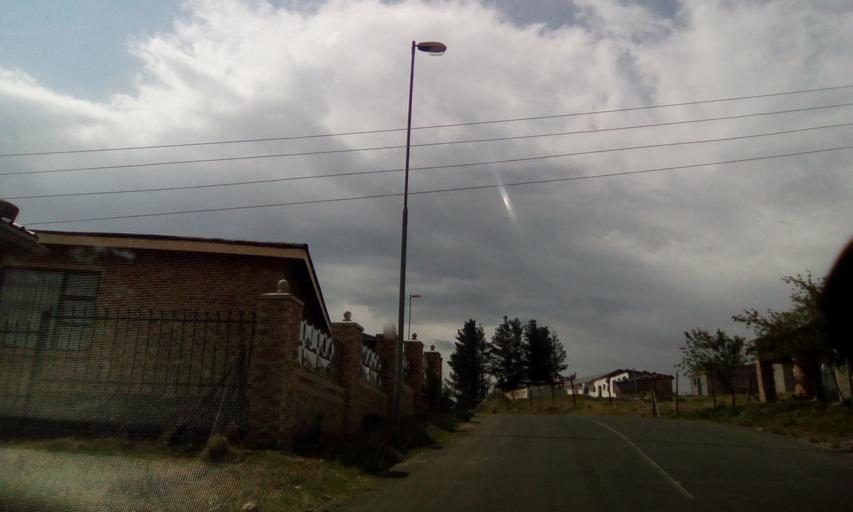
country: LS
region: Qacha's Nek
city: Qacha's Nek
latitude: -30.1163
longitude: 28.6795
